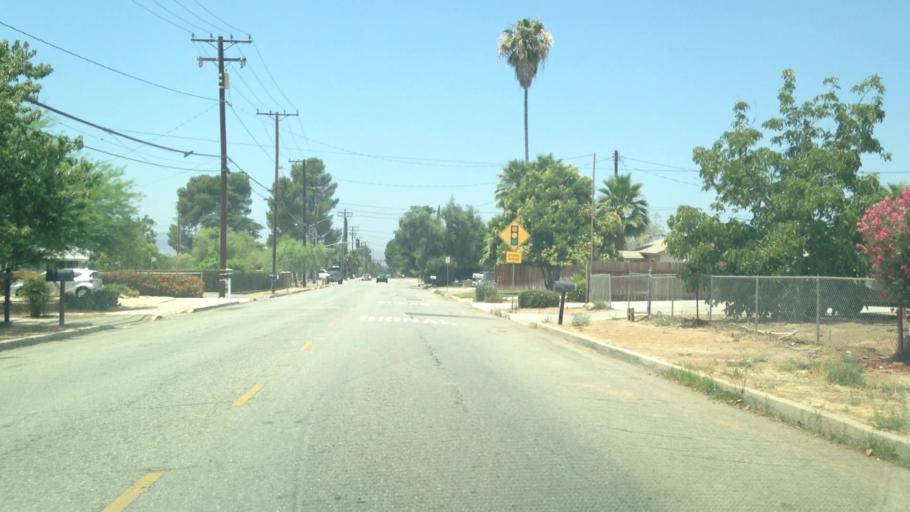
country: US
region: California
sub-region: San Bernardino County
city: Yucaipa
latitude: 34.0266
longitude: -117.0369
